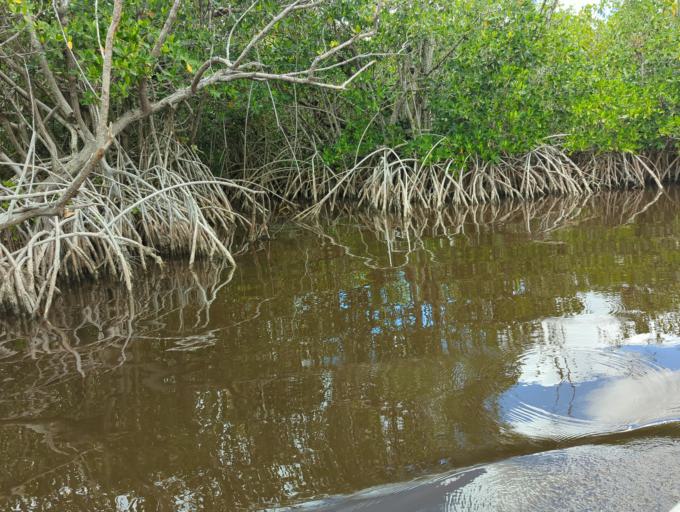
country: US
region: Florida
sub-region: Collier County
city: Marco
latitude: 25.9048
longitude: -81.3743
